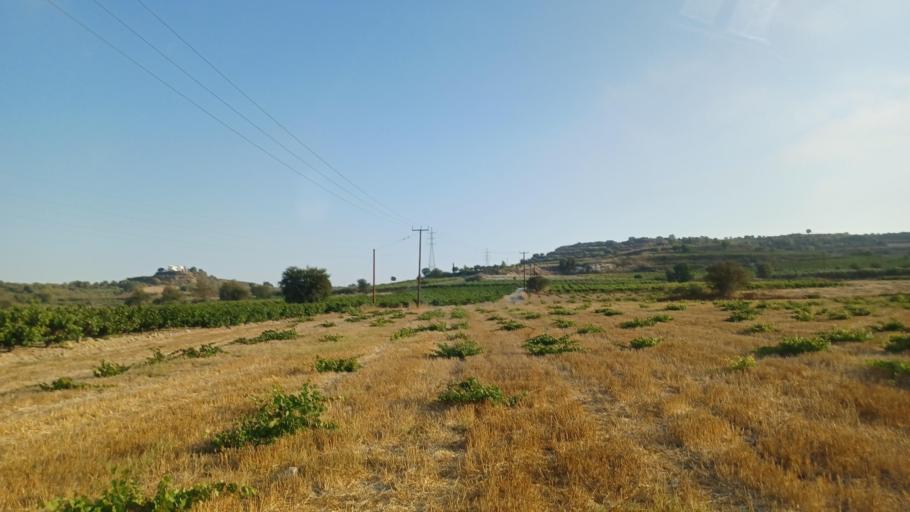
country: CY
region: Pafos
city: Tala
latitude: 34.8890
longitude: 32.4935
